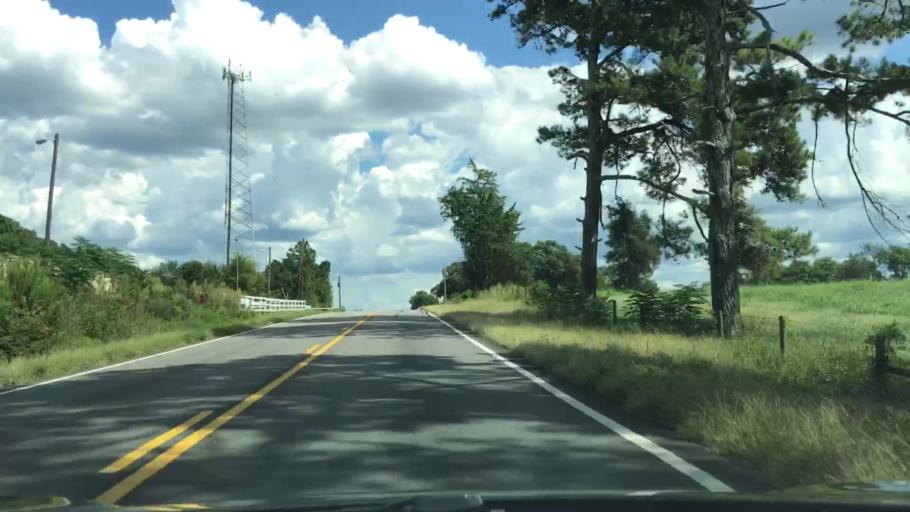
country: US
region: Georgia
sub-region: Greene County
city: Greensboro
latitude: 33.5661
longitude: -83.1528
